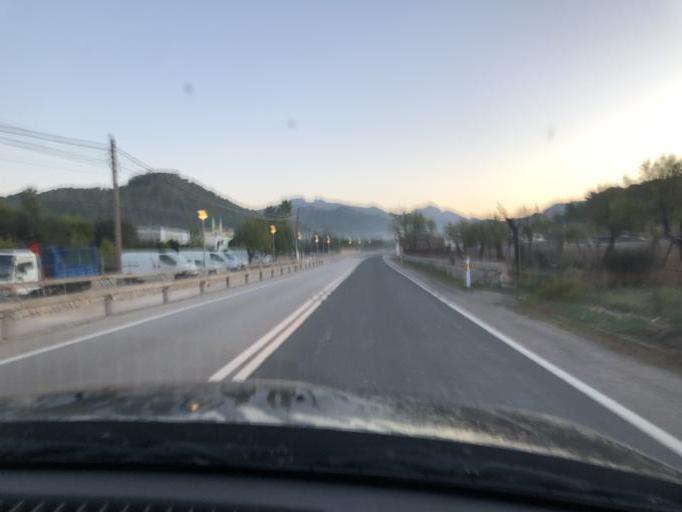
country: ES
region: Balearic Islands
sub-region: Illes Balears
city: Andratx
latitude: 39.5615
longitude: 2.4019
